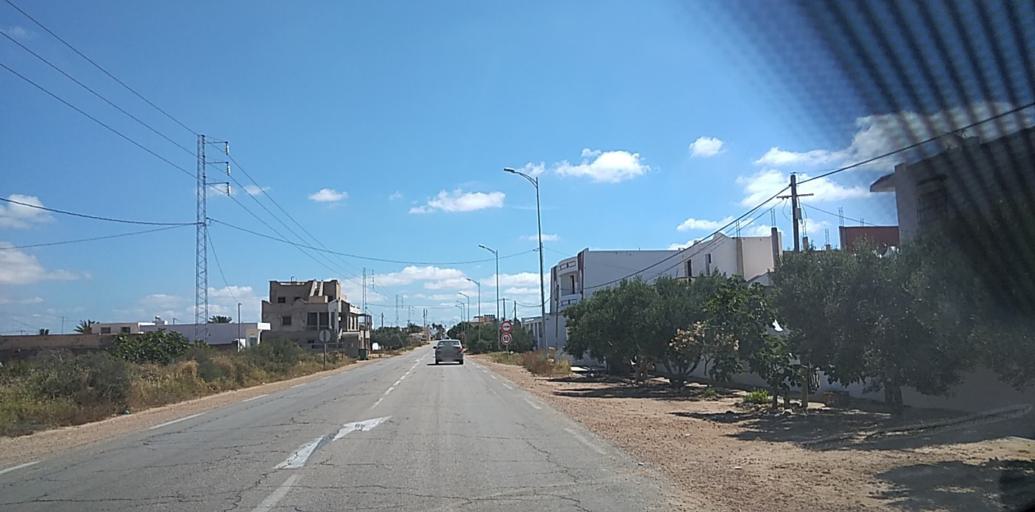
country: TN
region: Safaqis
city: Al Qarmadah
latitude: 34.6695
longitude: 11.1350
